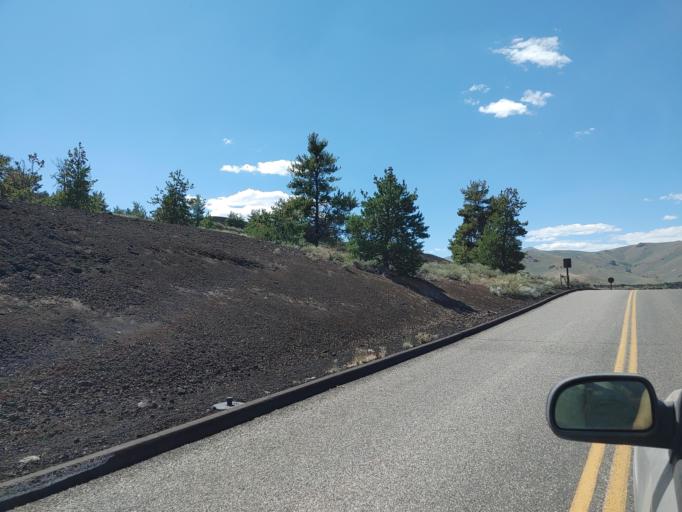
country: US
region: Idaho
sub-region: Butte County
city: Arco
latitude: 43.4554
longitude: -113.5583
